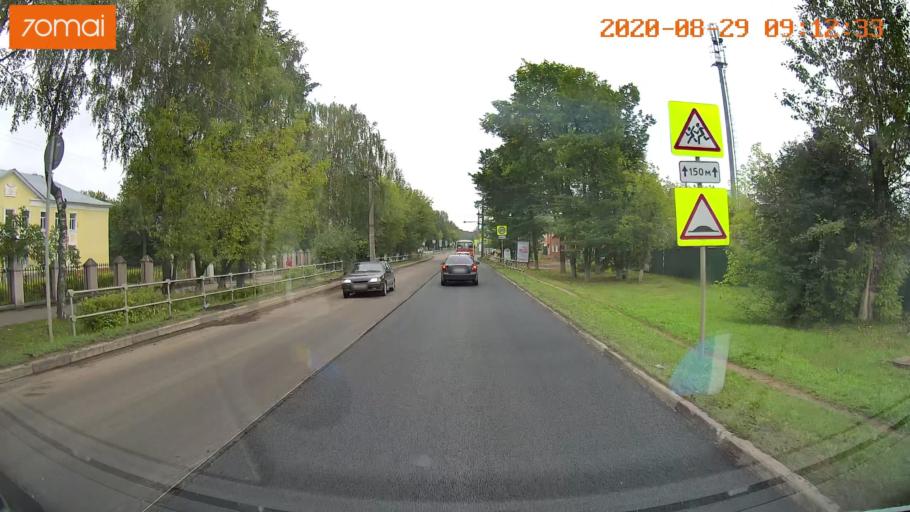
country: RU
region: Ivanovo
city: Kineshma
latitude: 57.4292
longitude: 42.0972
